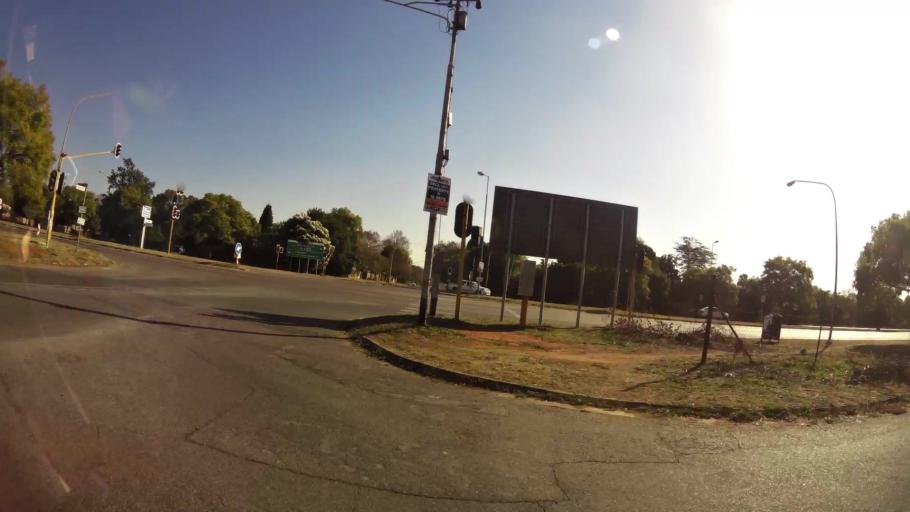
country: ZA
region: Gauteng
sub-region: City of Tshwane Metropolitan Municipality
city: Pretoria
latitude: -25.7278
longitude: 28.2588
